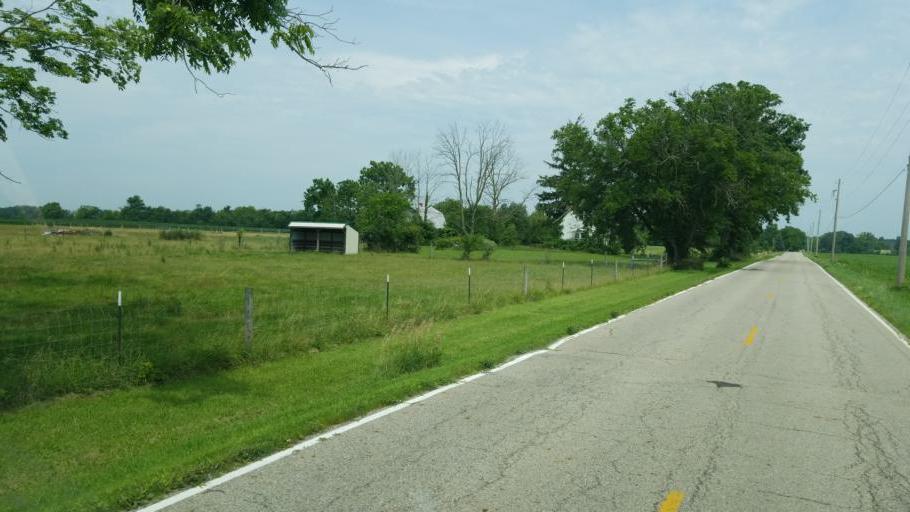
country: US
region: Ohio
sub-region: Madison County
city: West Jefferson
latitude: 39.8942
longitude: -83.2548
